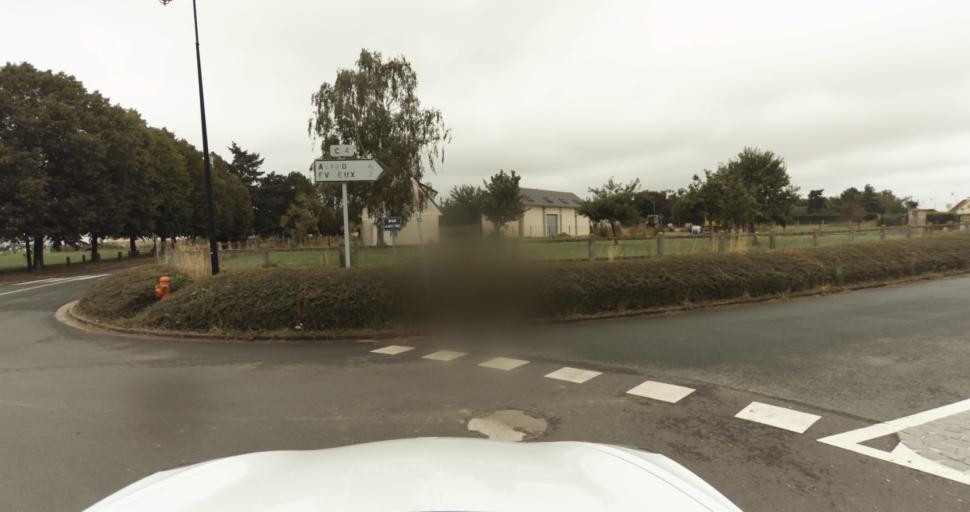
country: FR
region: Haute-Normandie
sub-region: Departement de l'Eure
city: Aviron
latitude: 49.0778
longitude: 1.0841
